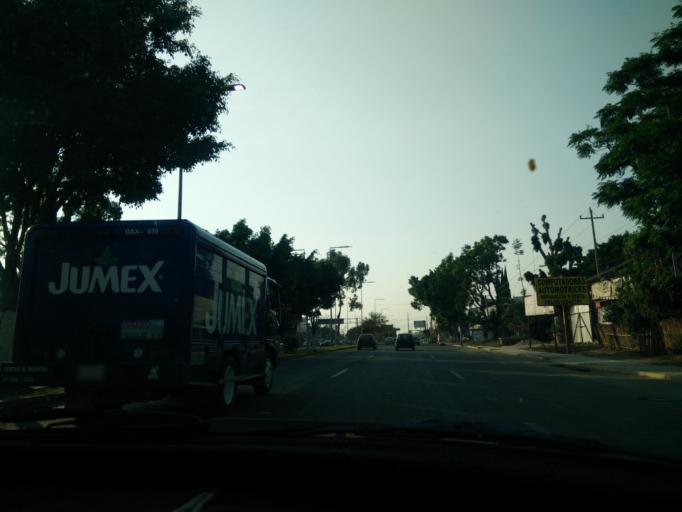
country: MX
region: Oaxaca
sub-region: Santa Maria Atzompa
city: San Jeronimo Yahuiche
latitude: 17.1201
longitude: -96.7623
